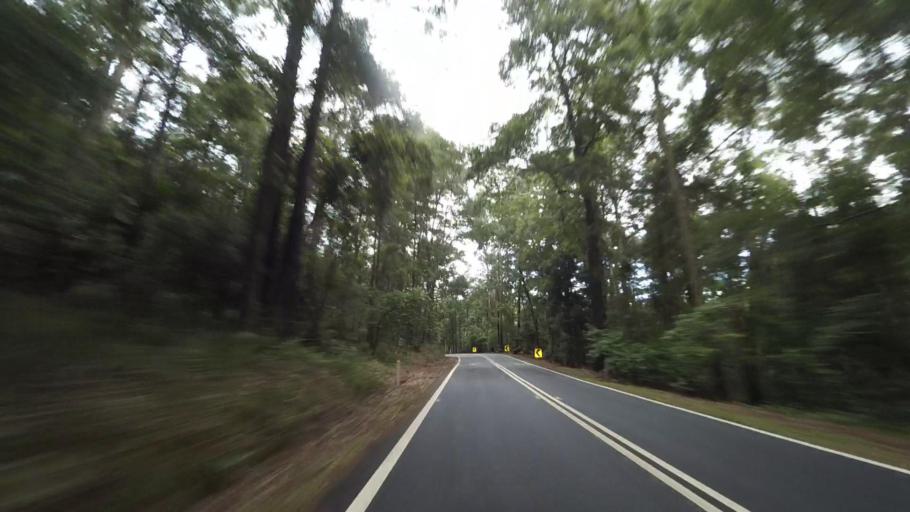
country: AU
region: New South Wales
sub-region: Wollongong
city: Helensburgh
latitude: -34.1628
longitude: 151.0155
